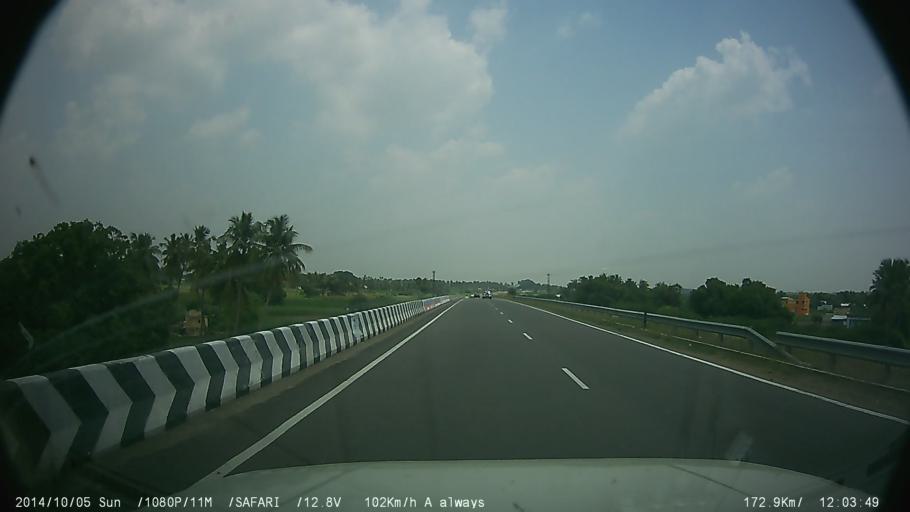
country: IN
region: Tamil Nadu
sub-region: Villupuram
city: Chinna Salem
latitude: 11.6394
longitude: 78.8684
